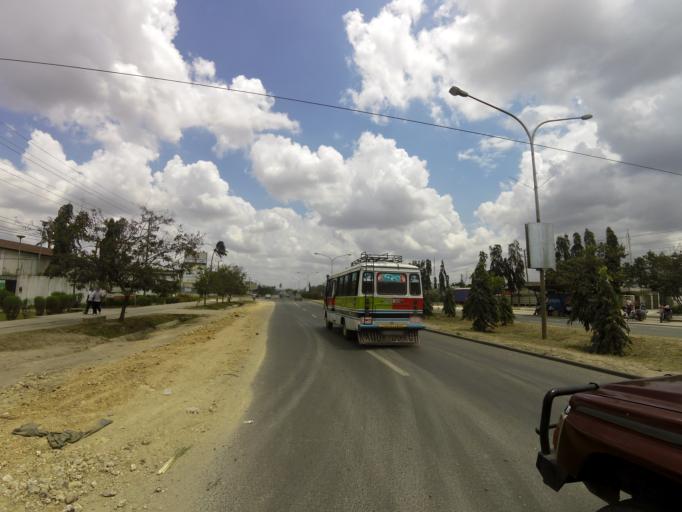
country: TZ
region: Dar es Salaam
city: Dar es Salaam
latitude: -6.8554
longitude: 39.2232
